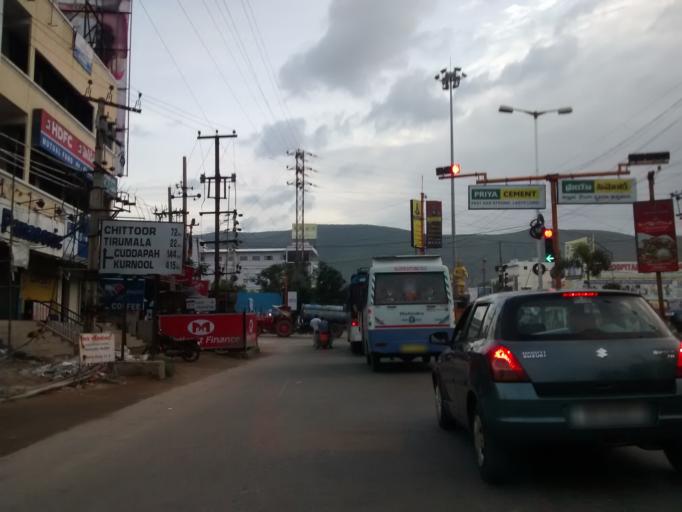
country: IN
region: Andhra Pradesh
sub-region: Chittoor
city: Tirupati
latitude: 13.6414
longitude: 79.4276
